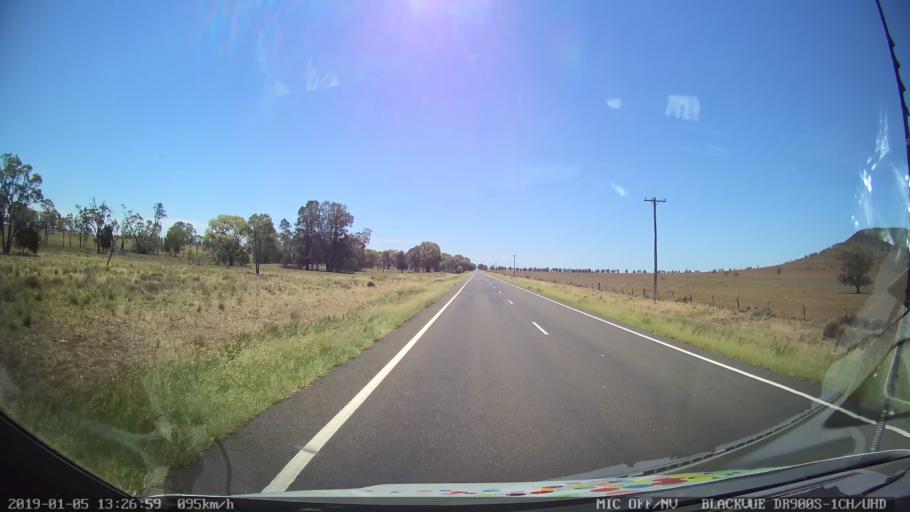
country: AU
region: New South Wales
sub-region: Gunnedah
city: Gunnedah
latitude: -31.0484
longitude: 150.0231
